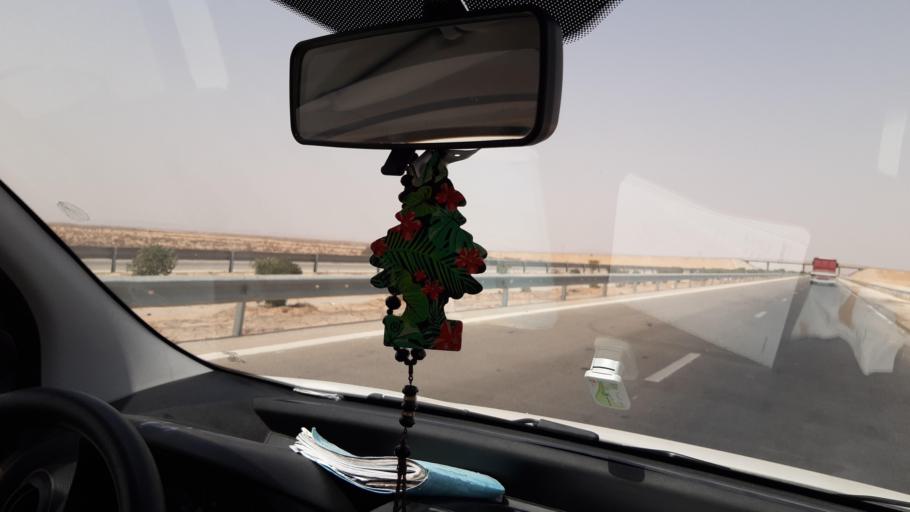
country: TN
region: Qabis
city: Gabes
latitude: 33.9296
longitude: 9.9653
